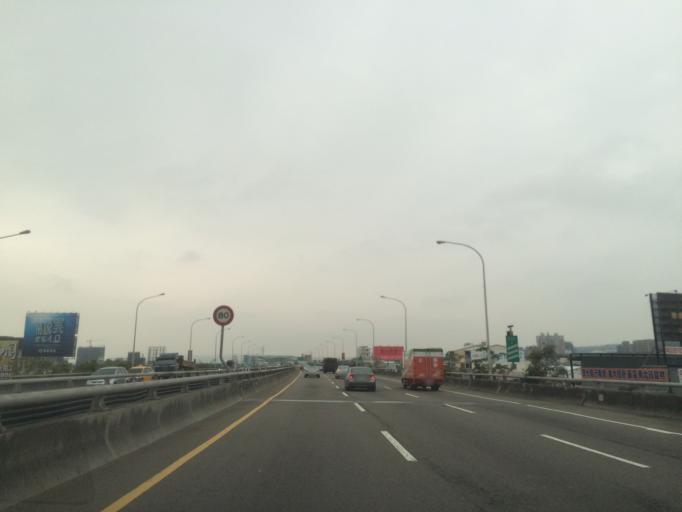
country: TW
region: Taiwan
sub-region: Taichung City
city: Taichung
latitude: 24.1579
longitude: 120.6261
